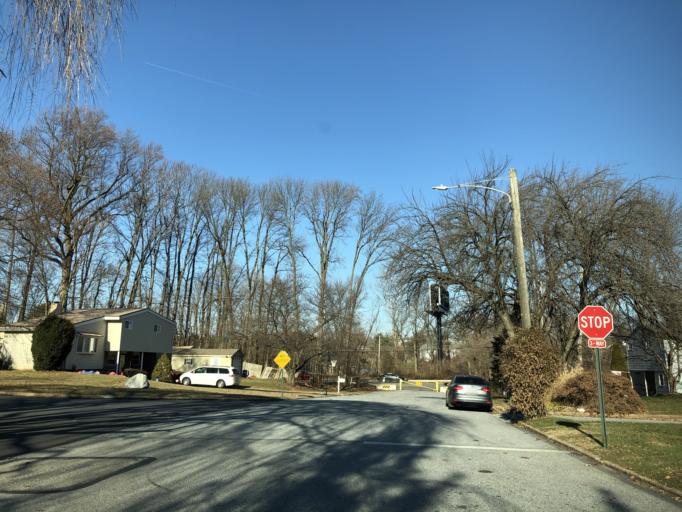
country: US
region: Pennsylvania
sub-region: Delaware County
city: Boothwyn
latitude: 39.8481
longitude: -75.4398
